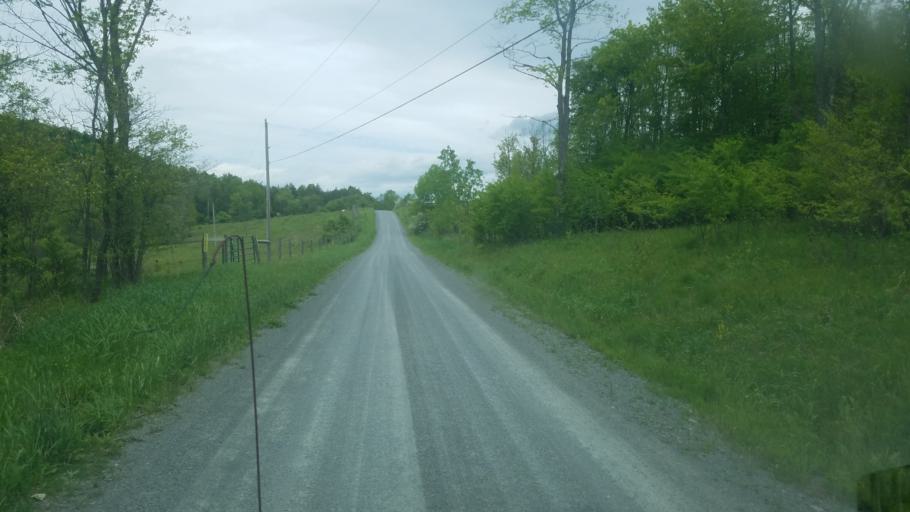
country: US
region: Pennsylvania
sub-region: Tioga County
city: Westfield
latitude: 41.8443
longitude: -77.6027
